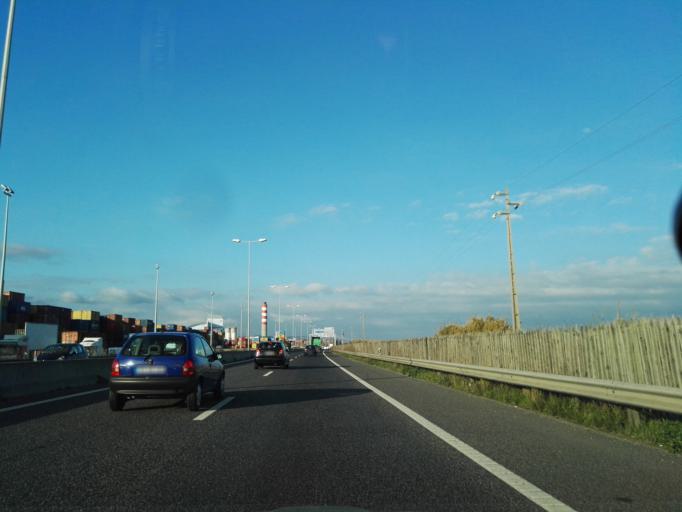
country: PT
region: Lisbon
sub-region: Loures
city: Sao Joao da Talha
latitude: 38.8207
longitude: -9.0856
